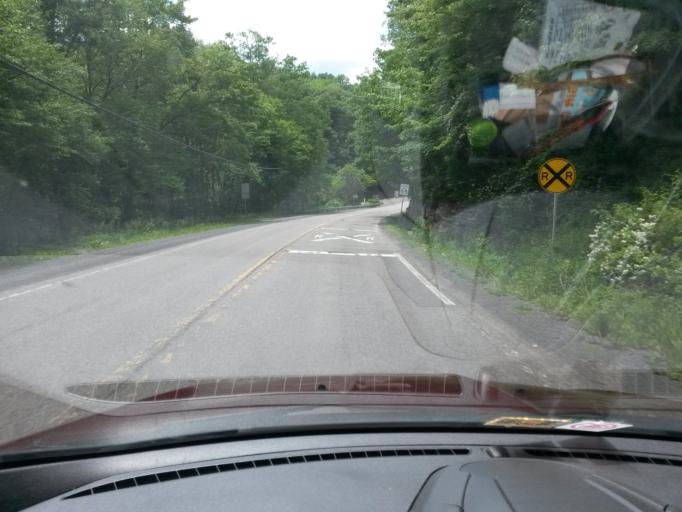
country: US
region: West Virginia
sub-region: Greenbrier County
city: Rainelle
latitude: 38.0547
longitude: -80.7109
